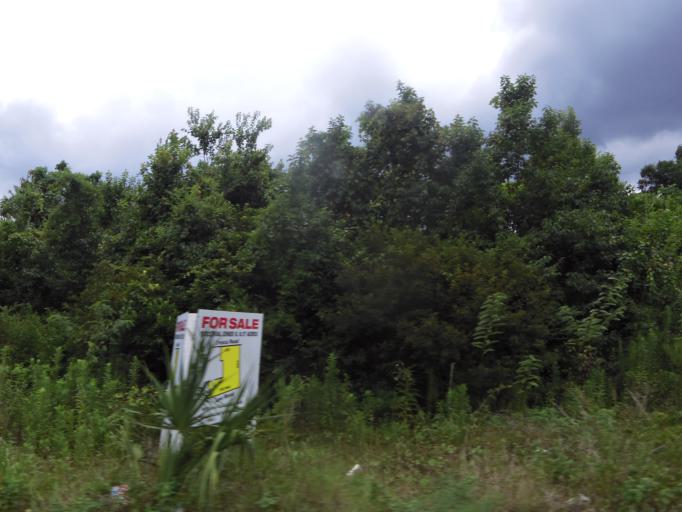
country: US
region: Florida
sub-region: Duval County
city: Jacksonville
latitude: 30.3320
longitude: -81.5371
